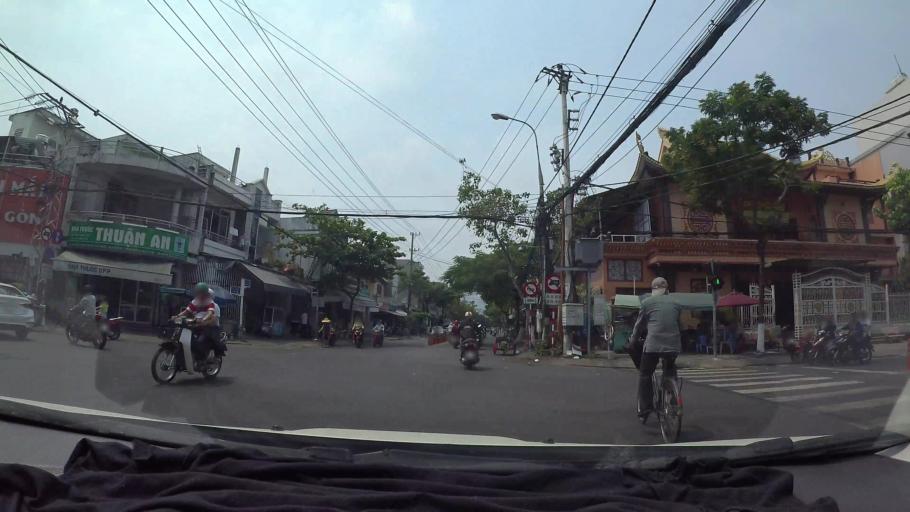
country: VN
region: Da Nang
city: Thanh Khe
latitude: 16.0713
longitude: 108.2013
